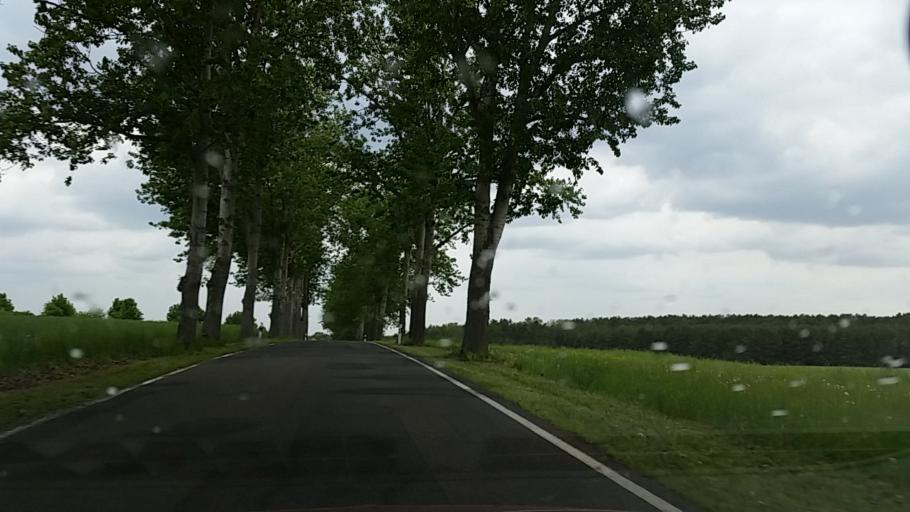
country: DE
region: Brandenburg
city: Rauen
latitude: 52.3193
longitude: 13.9614
